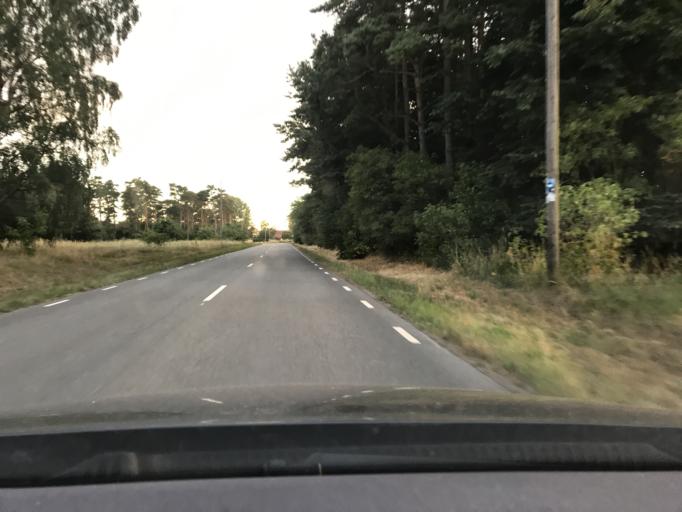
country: SE
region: Skane
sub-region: Simrishamns Kommun
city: Simrishamn
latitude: 55.4345
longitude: 14.2281
